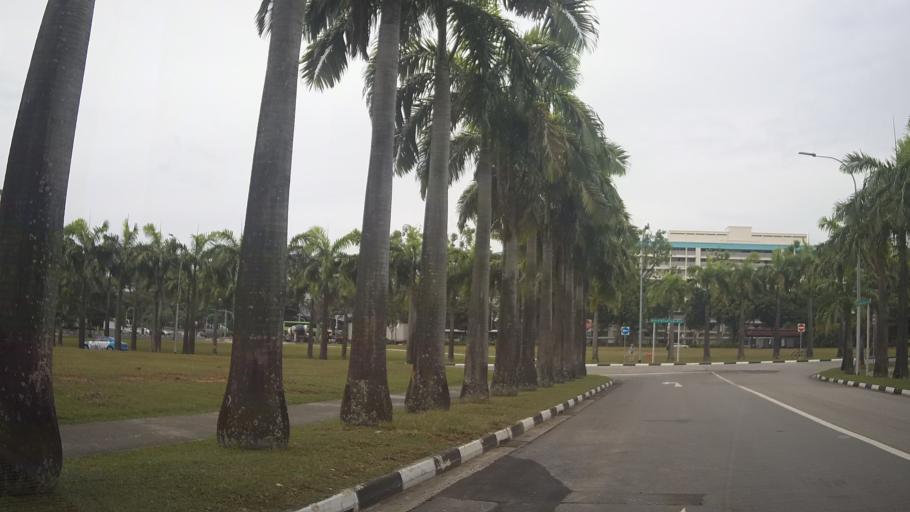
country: MY
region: Johor
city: Johor Bahru
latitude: 1.4393
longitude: 103.7849
